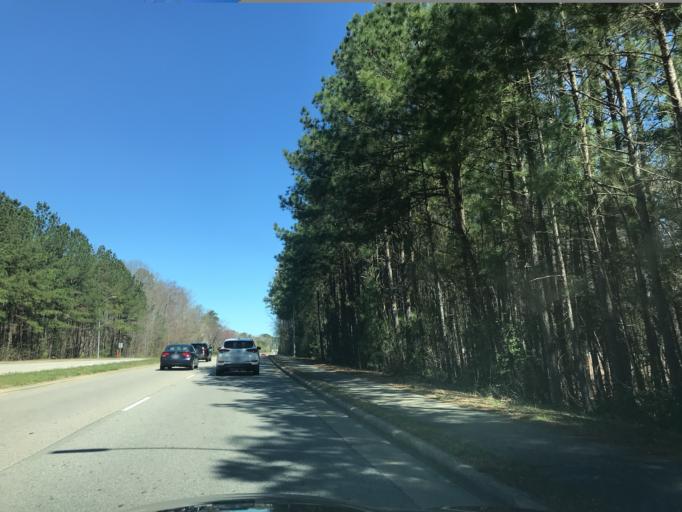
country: US
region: North Carolina
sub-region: Wake County
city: Garner
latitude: 35.7106
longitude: -78.6412
